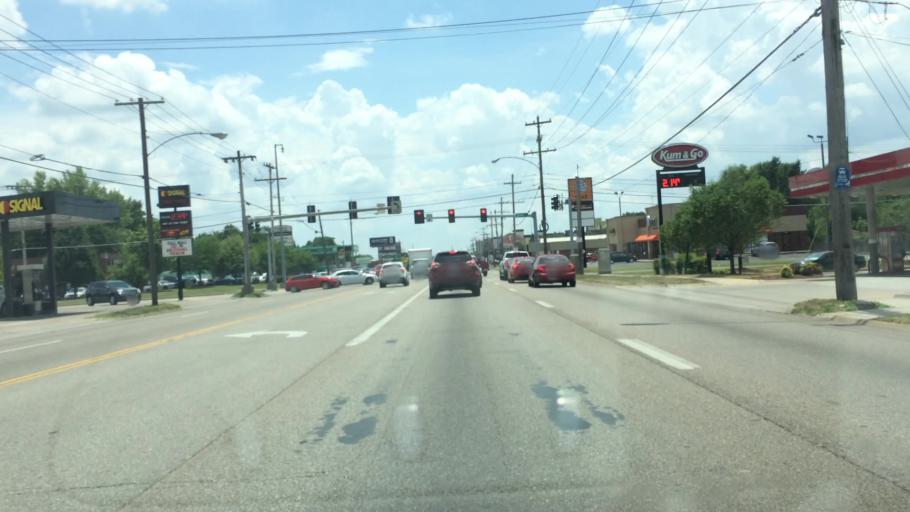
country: US
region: Missouri
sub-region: Greene County
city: Springfield
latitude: 37.1970
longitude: -93.2621
